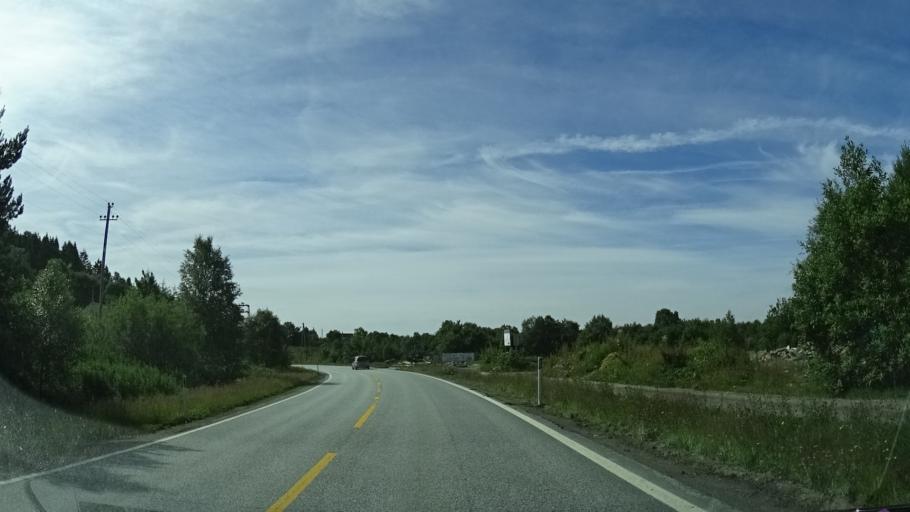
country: NO
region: Hordaland
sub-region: Bomlo
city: Mosterhamn
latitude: 59.6718
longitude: 5.4584
